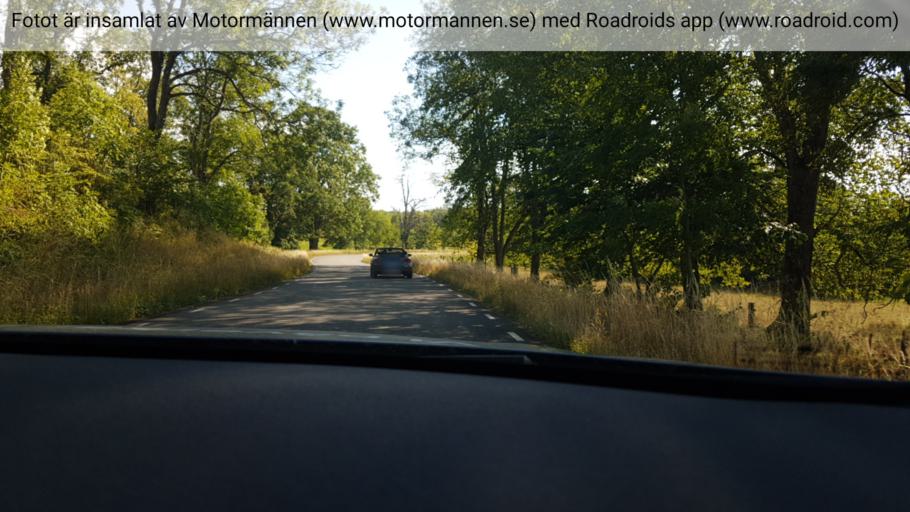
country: SE
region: Vaestra Goetaland
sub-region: Gotene Kommun
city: Kallby
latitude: 58.5444
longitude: 13.3302
